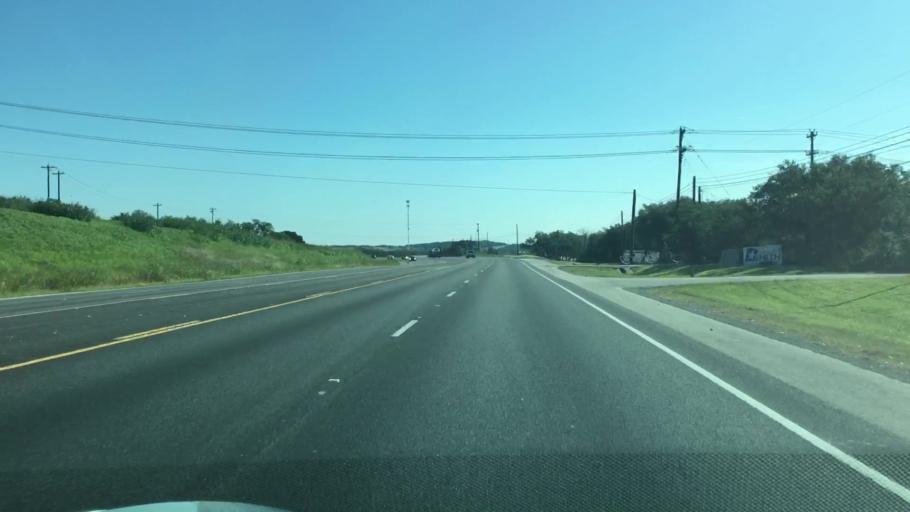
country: US
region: Texas
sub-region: Hays County
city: Dripping Springs
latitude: 30.1922
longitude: -98.0679
